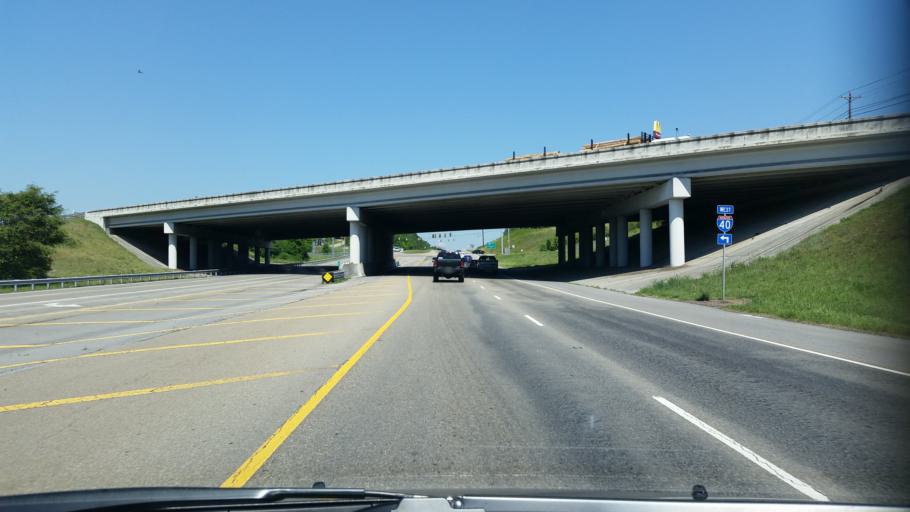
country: US
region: Tennessee
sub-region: Jefferson County
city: Dandridge
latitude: 36.0382
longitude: -83.4393
